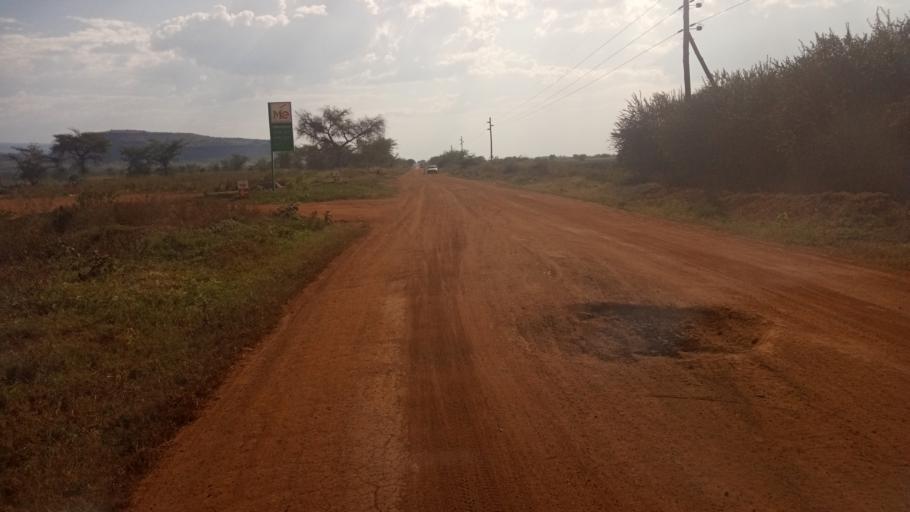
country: UG
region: Eastern Region
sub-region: Kween District
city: Binyin
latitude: 1.5240
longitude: 34.4866
